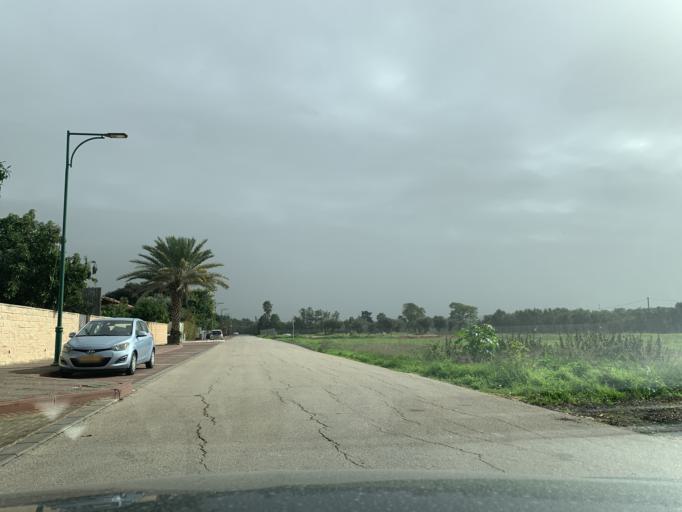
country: IL
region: Central District
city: Jaljulya
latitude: 32.1570
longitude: 34.9396
